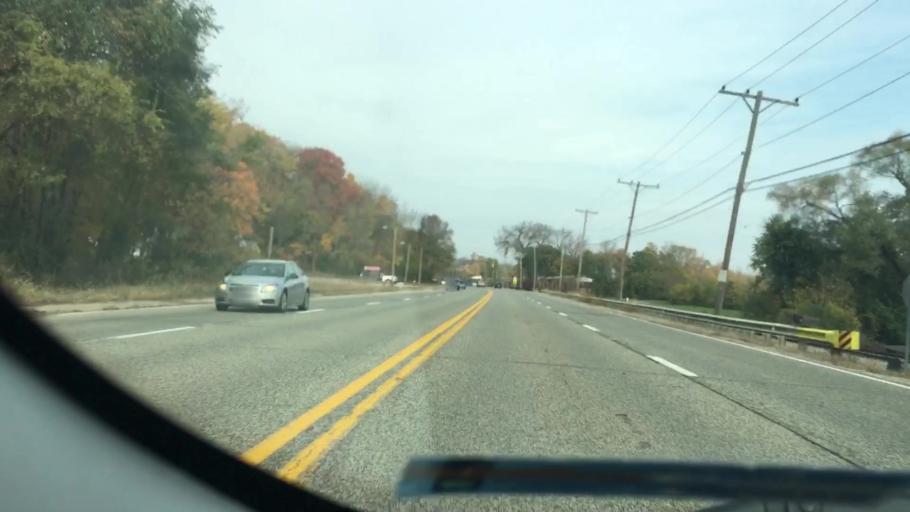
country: US
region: Illinois
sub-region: Peoria County
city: Peoria Heights
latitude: 40.7413
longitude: -89.5541
